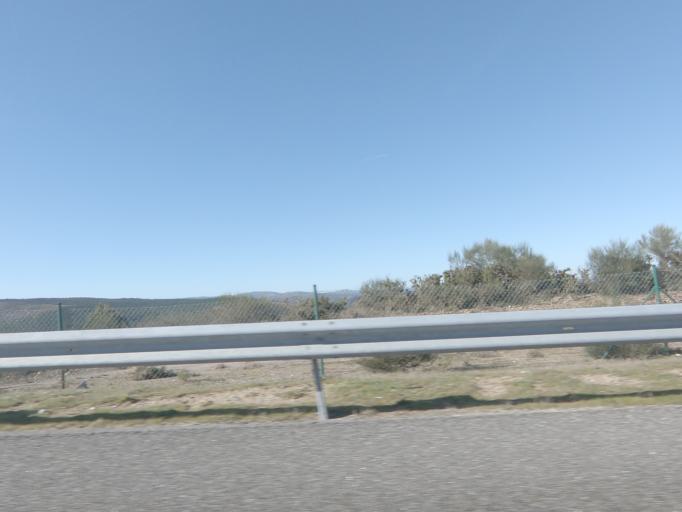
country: ES
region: Galicia
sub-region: Provincia de Pontevedra
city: Dozon
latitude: 42.5739
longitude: -8.0615
